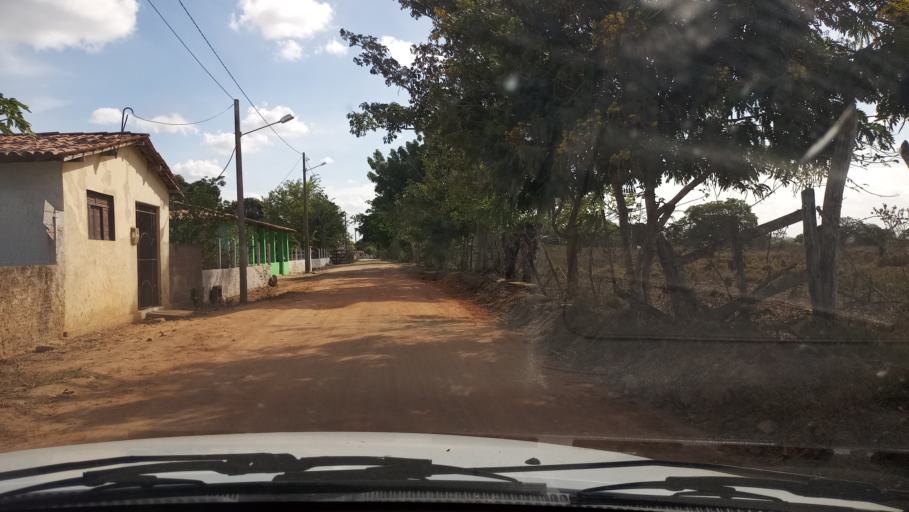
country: BR
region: Rio Grande do Norte
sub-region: Goianinha
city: Goianinha
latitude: -6.3178
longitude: -35.3079
